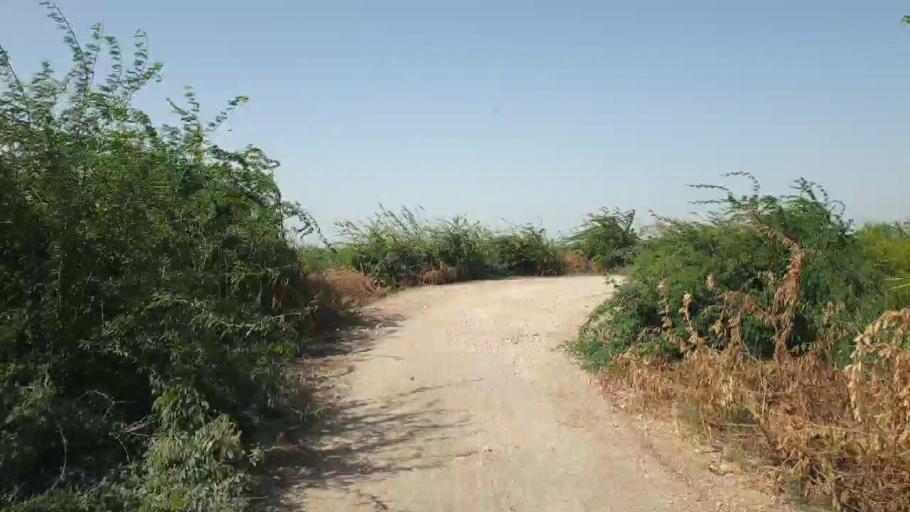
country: PK
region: Sindh
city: Tando Bago
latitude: 24.7500
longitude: 69.0288
